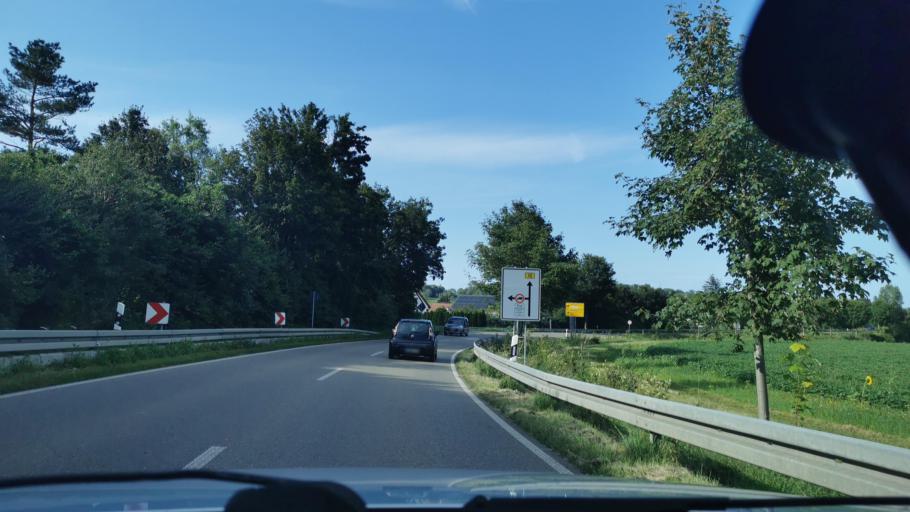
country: DE
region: Baden-Wuerttemberg
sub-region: Regierungsbezirk Stuttgart
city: Schlierbach
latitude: 48.6884
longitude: 9.5032
